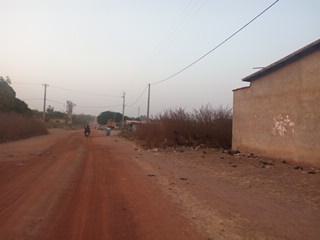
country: BJ
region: Borgou
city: Parakou
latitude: 9.3161
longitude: 2.6015
